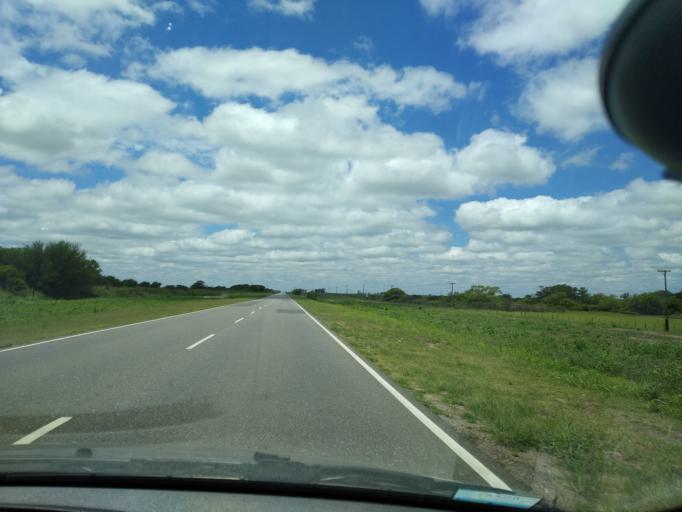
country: AR
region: Cordoba
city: Toledo
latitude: -31.6471
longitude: -64.0685
